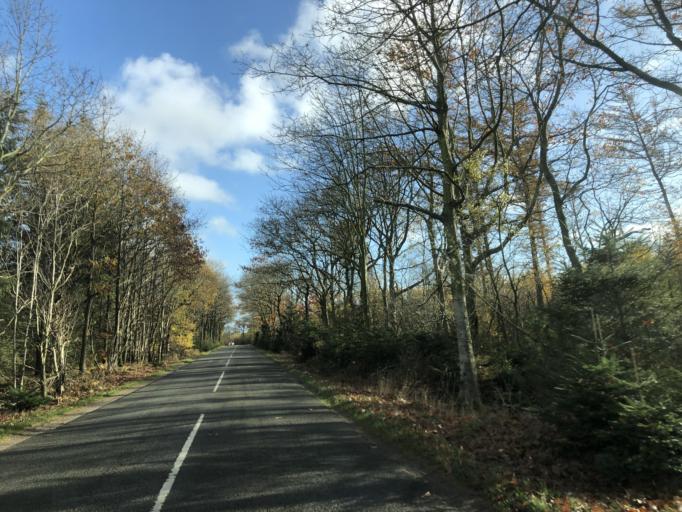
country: DK
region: Central Jutland
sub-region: Ringkobing-Skjern Kommune
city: Ringkobing
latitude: 56.1416
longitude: 8.3071
